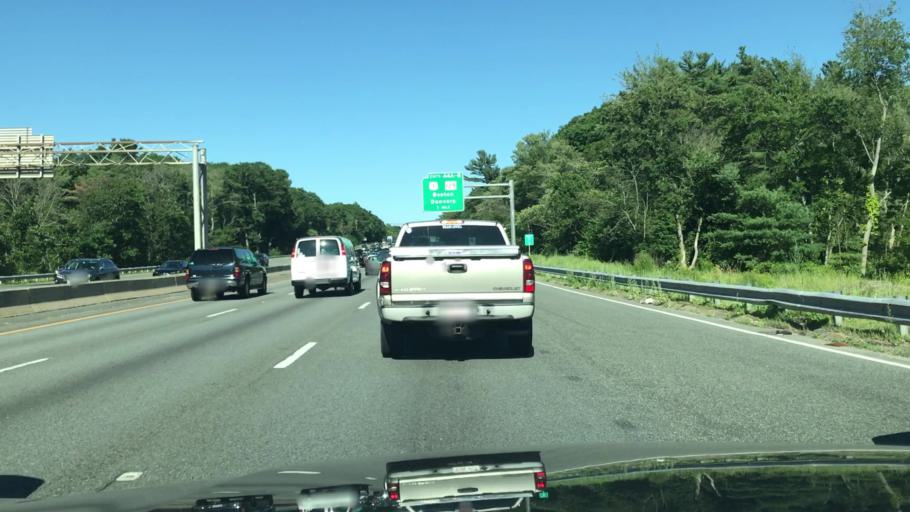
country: US
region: Massachusetts
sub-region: Essex County
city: Lynnfield
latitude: 42.5142
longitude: -71.0247
